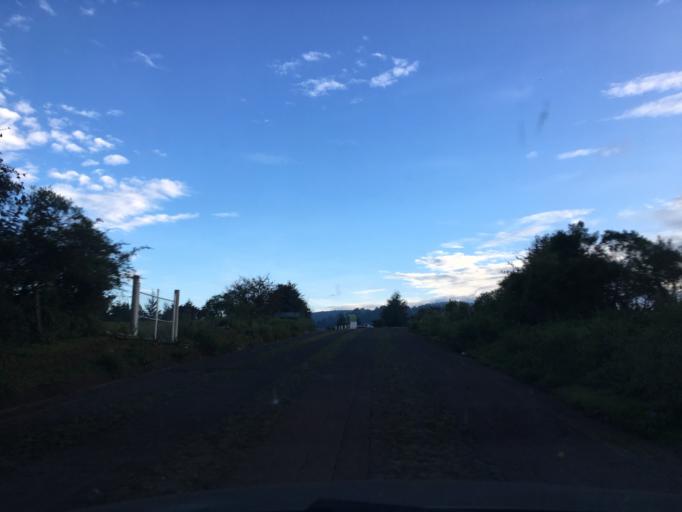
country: MX
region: Michoacan
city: Villa Escalante
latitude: 19.4231
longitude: -101.7105
